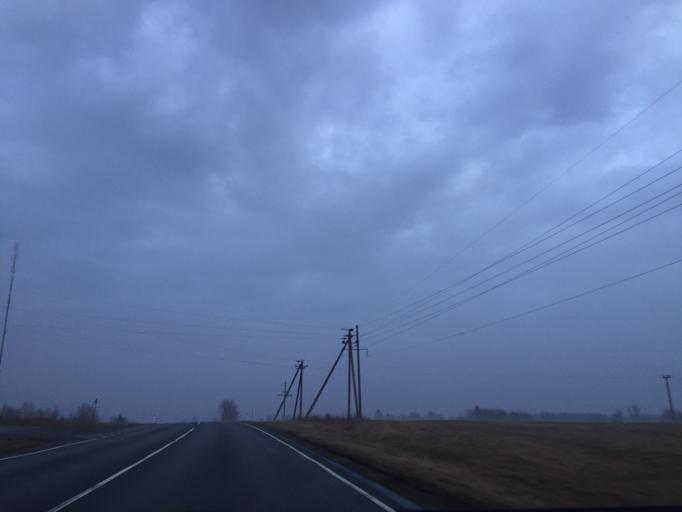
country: EE
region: Laeaene
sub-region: Lihula vald
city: Lihula
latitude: 58.6782
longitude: 23.8154
